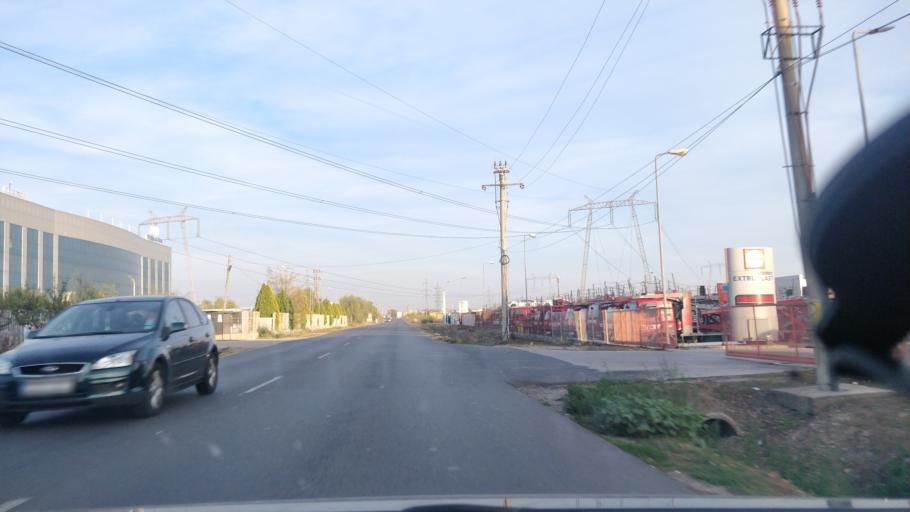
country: RO
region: Ilfov
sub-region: Comuna Ciorogarla
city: Ciorogarla
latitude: 44.4405
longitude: 25.9166
